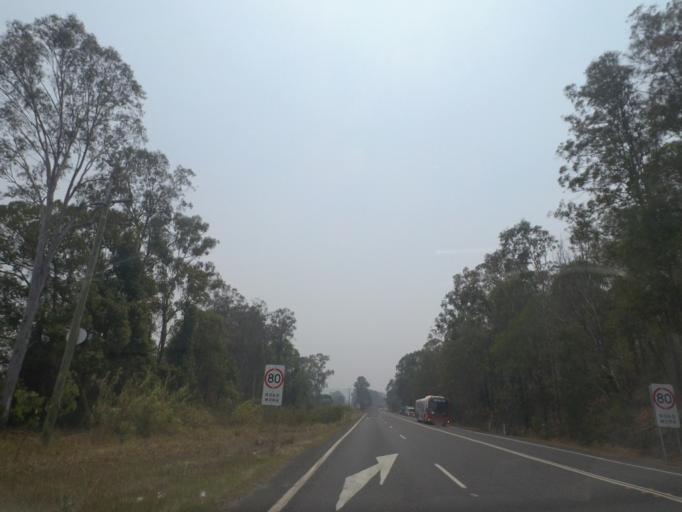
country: AU
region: New South Wales
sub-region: Clarence Valley
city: Maclean
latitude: -29.5567
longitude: 153.1513
